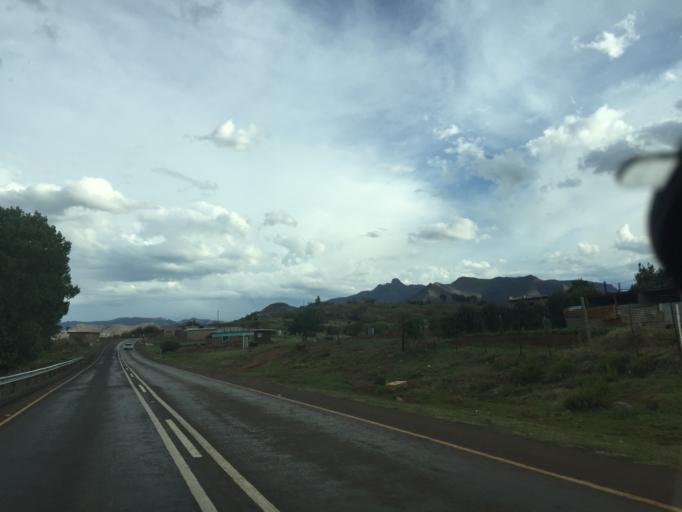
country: LS
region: Berea
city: Teyateyaneng
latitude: -29.1487
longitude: 28.0059
